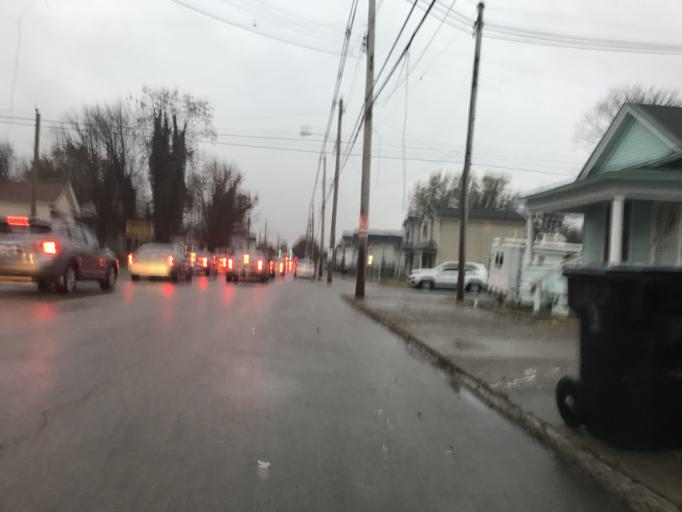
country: US
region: Kentucky
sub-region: Jefferson County
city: Louisville
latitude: 38.2387
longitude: -85.7406
